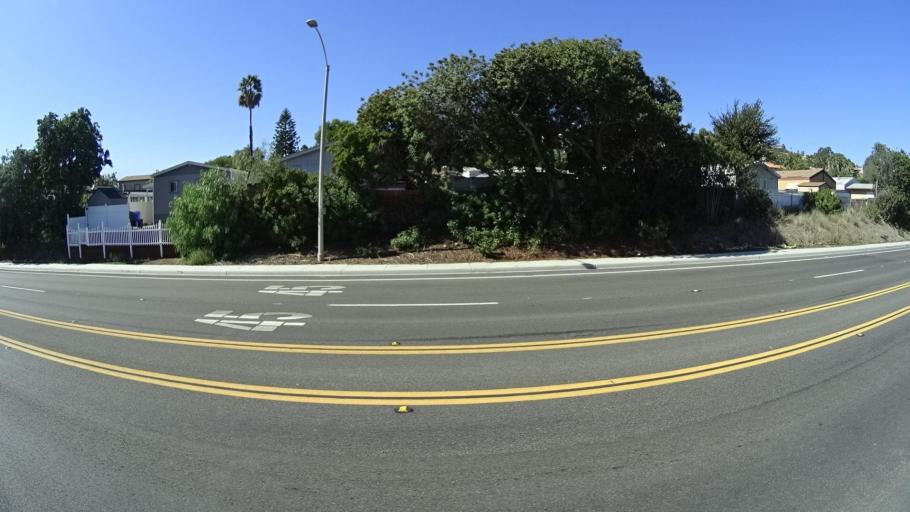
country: US
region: California
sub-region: San Diego County
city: La Presa
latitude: 32.7102
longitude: -116.9827
